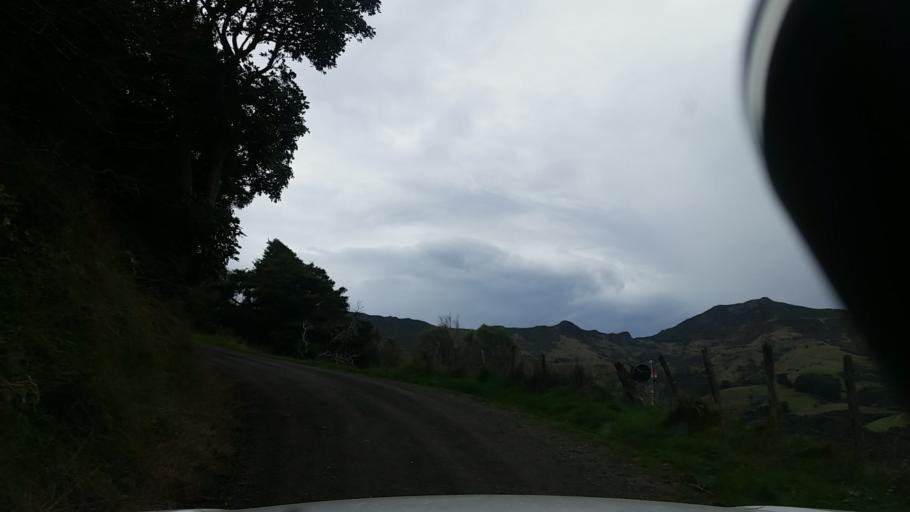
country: NZ
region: Canterbury
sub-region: Christchurch City
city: Christchurch
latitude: -43.7972
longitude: 172.9754
